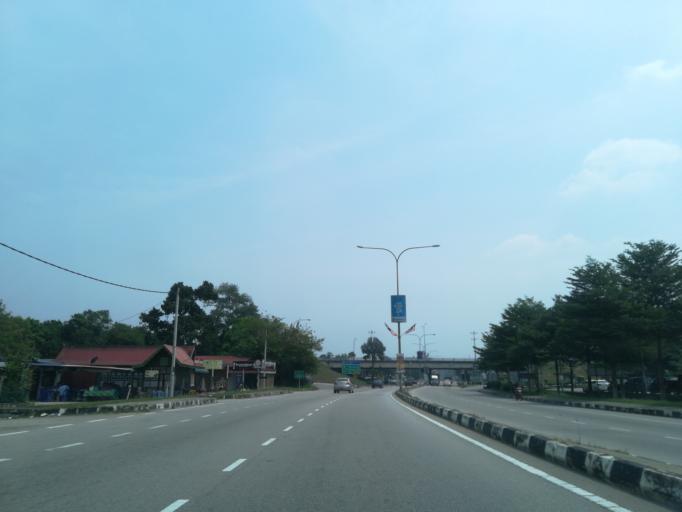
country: MY
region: Kedah
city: Kulim
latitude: 5.4188
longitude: 100.5381
